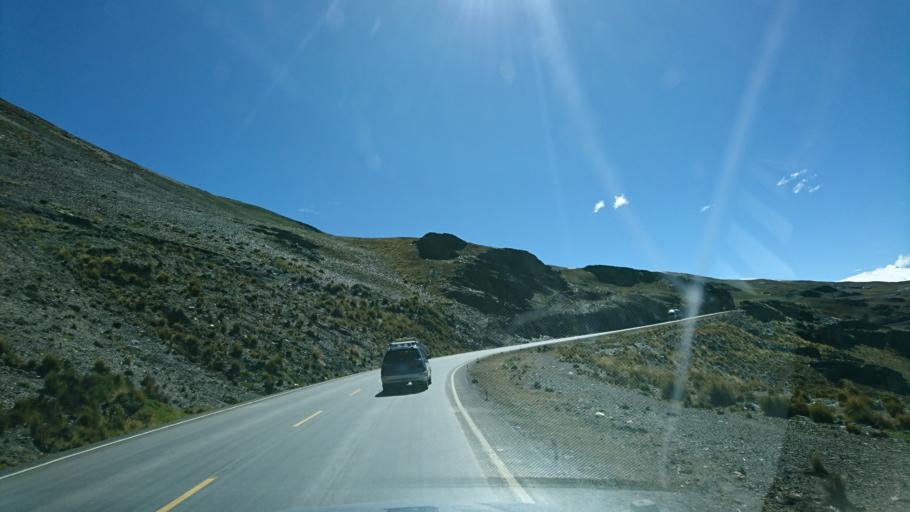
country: BO
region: La Paz
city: La Paz
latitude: -16.3788
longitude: -68.0440
